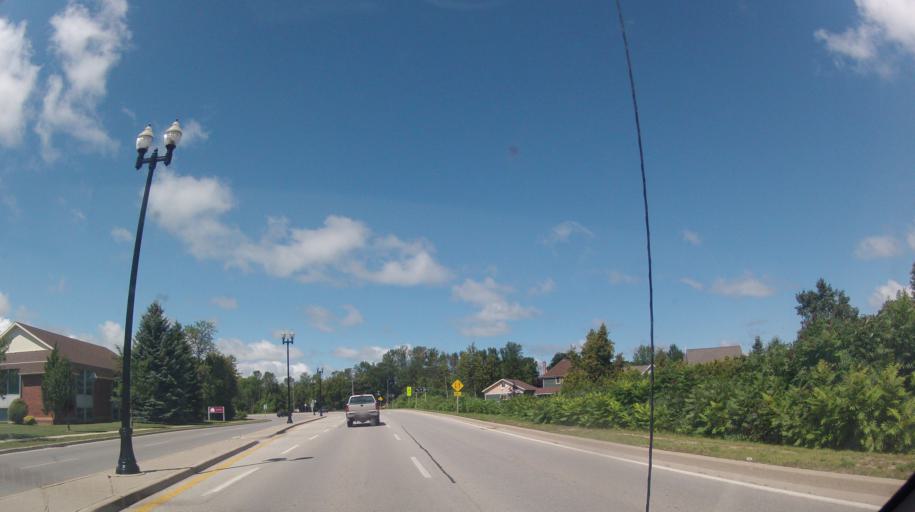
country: CA
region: Ontario
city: Collingwood
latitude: 44.5063
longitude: -80.2043
